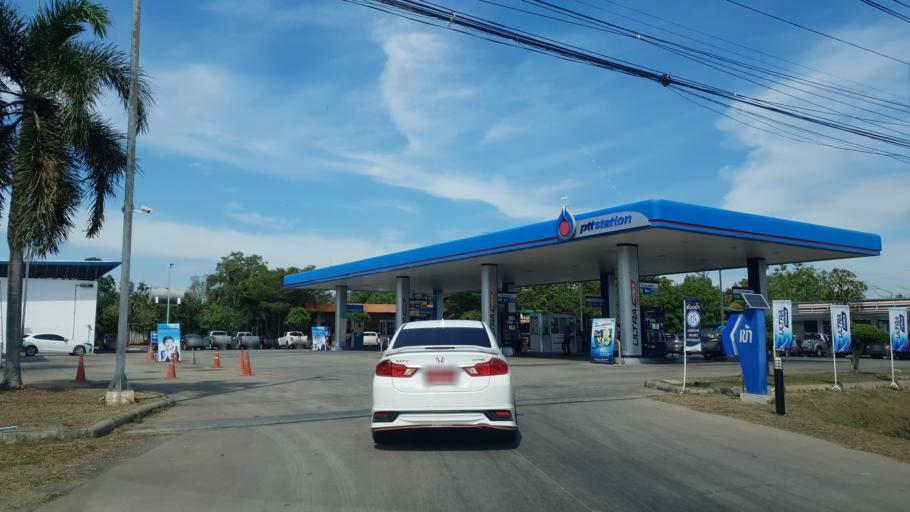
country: TH
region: Phitsanulok
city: Wang Thong
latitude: 16.8569
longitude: 100.3509
